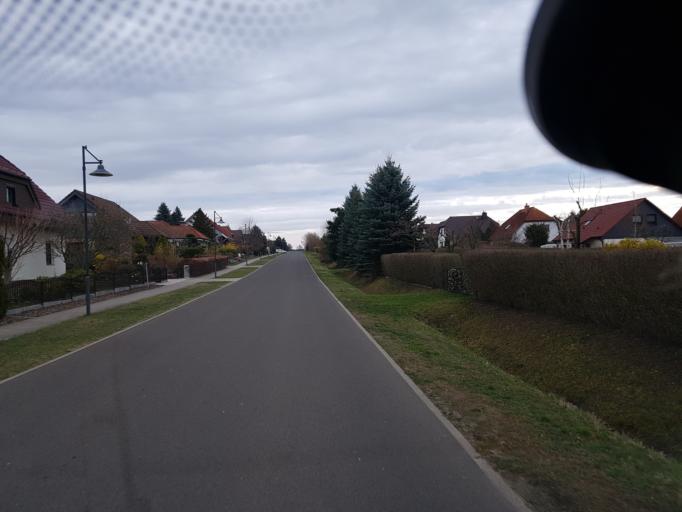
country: DE
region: Brandenburg
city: Mixdorf
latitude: 52.1980
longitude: 14.4002
